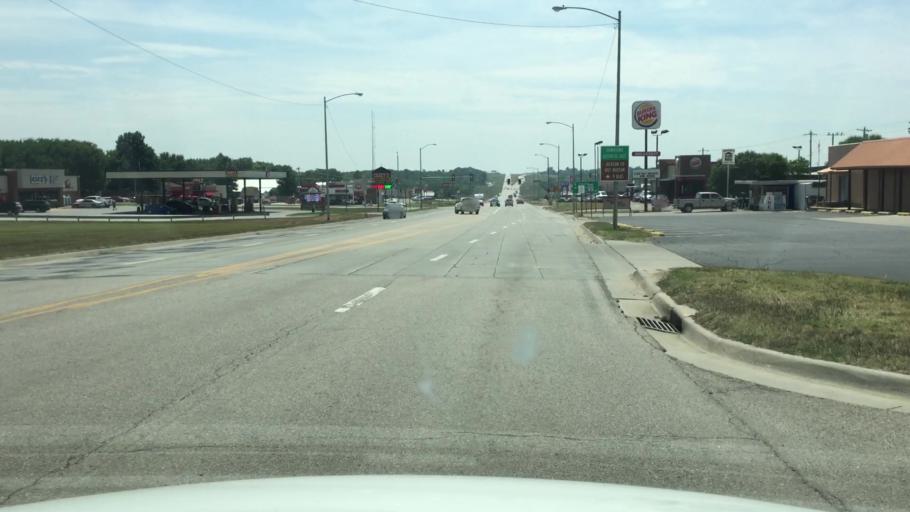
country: US
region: Kansas
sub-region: Jackson County
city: Holton
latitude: 39.4649
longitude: -95.7480
